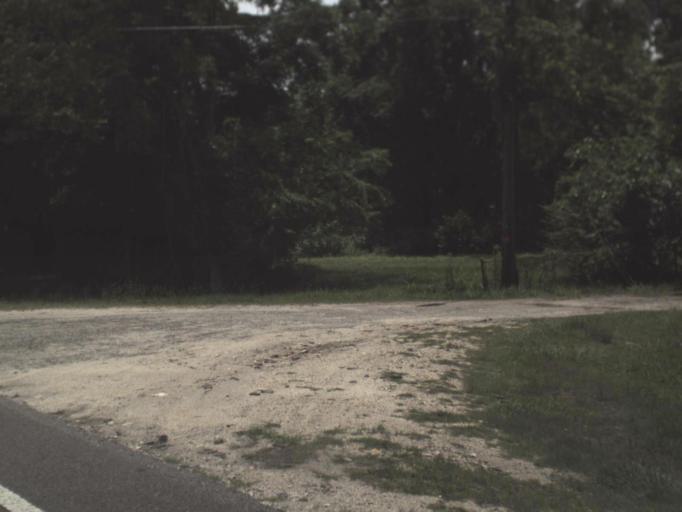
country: US
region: Florida
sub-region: Duval County
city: Jacksonville
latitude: 30.3761
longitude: -81.7274
